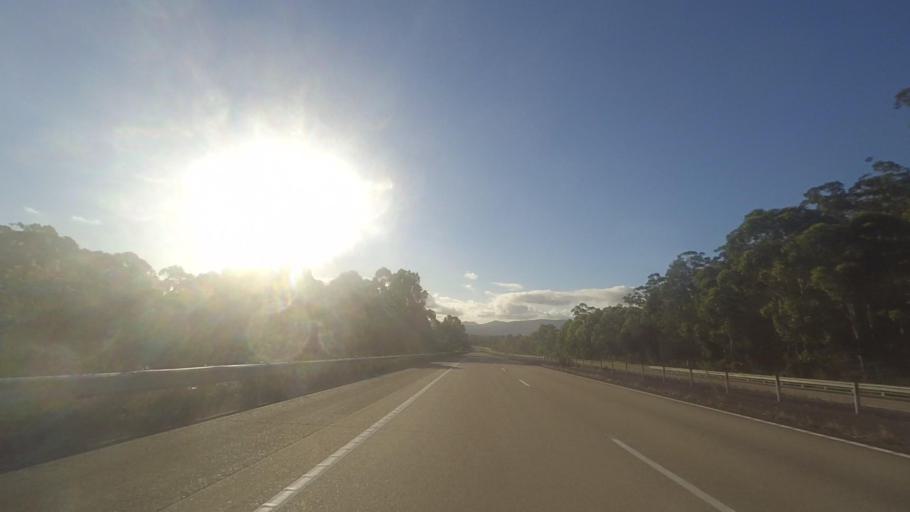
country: AU
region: New South Wales
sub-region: Great Lakes
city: Bulahdelah
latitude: -32.3873
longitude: 152.2419
